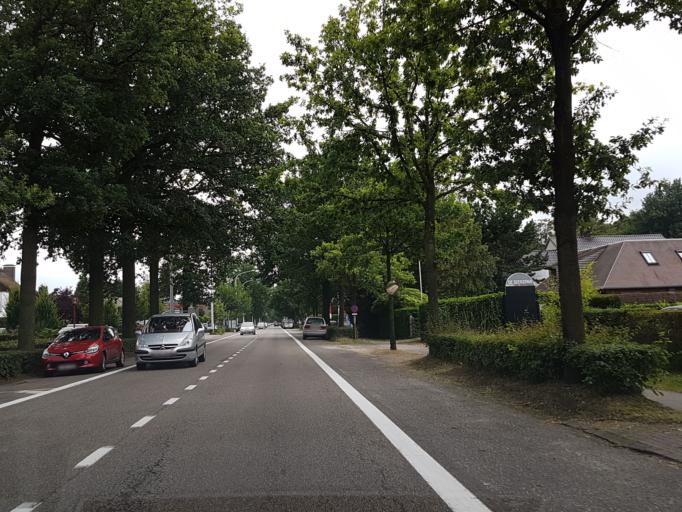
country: BE
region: Flanders
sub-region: Provincie Antwerpen
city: Brasschaat
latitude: 51.3069
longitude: 4.5065
